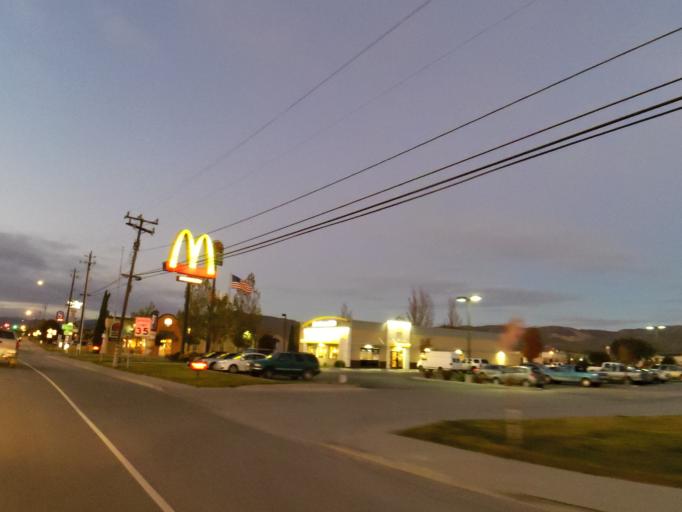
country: US
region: California
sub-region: Monterey County
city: Soledad
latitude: 36.4177
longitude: -121.3218
